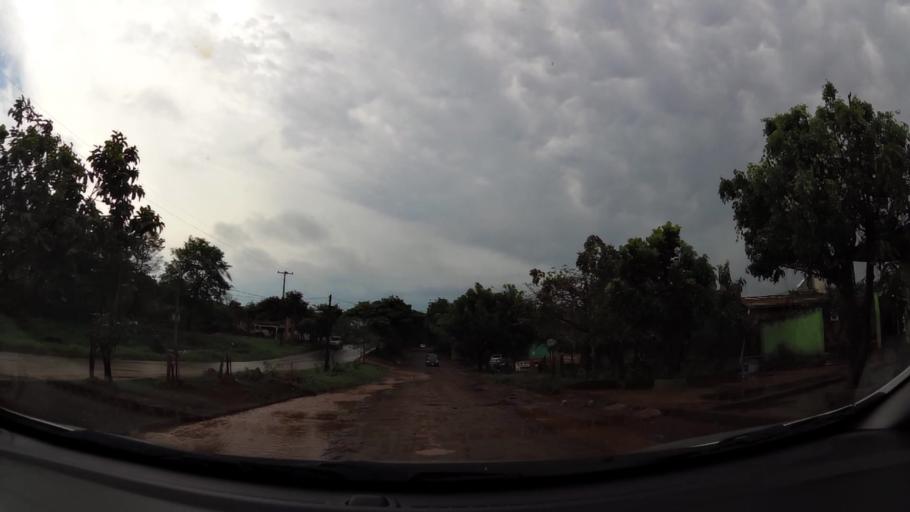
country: PY
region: Alto Parana
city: Presidente Franco
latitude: -25.5305
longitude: -54.6683
